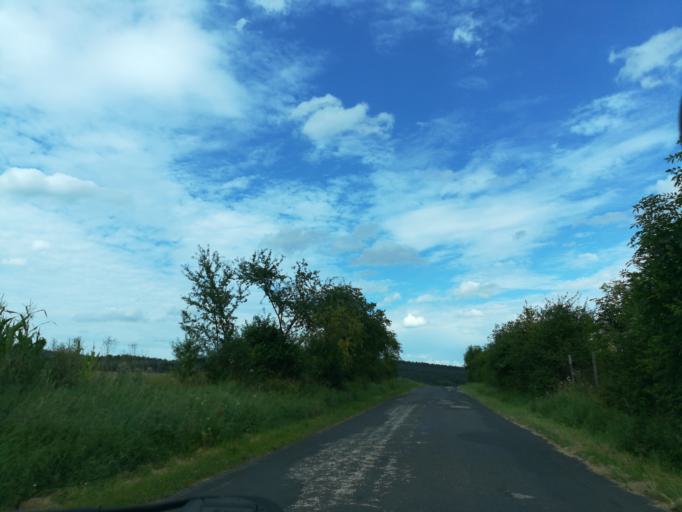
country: CZ
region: Kralovehradecky
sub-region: Okres Jicin
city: Zeleznice
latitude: 50.4694
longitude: 15.3996
